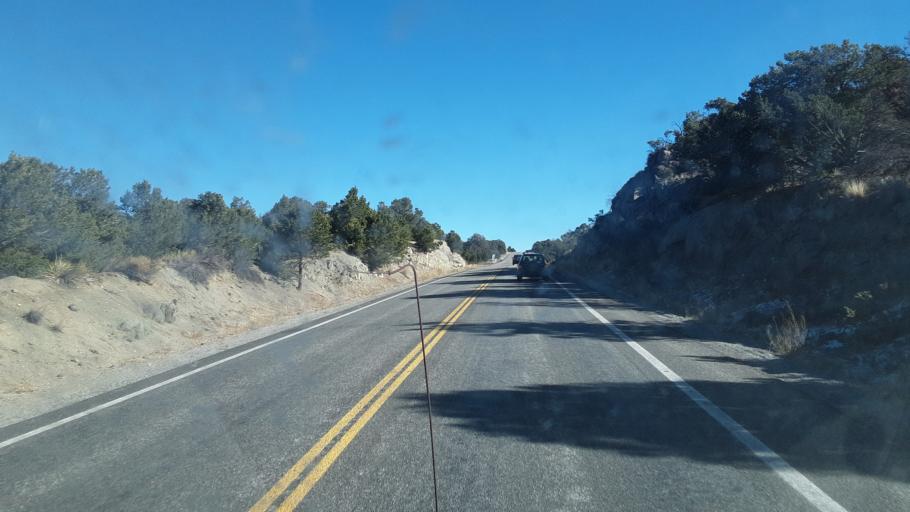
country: US
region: Colorado
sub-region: Chaffee County
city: Buena Vista
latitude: 38.8161
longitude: -106.0816
